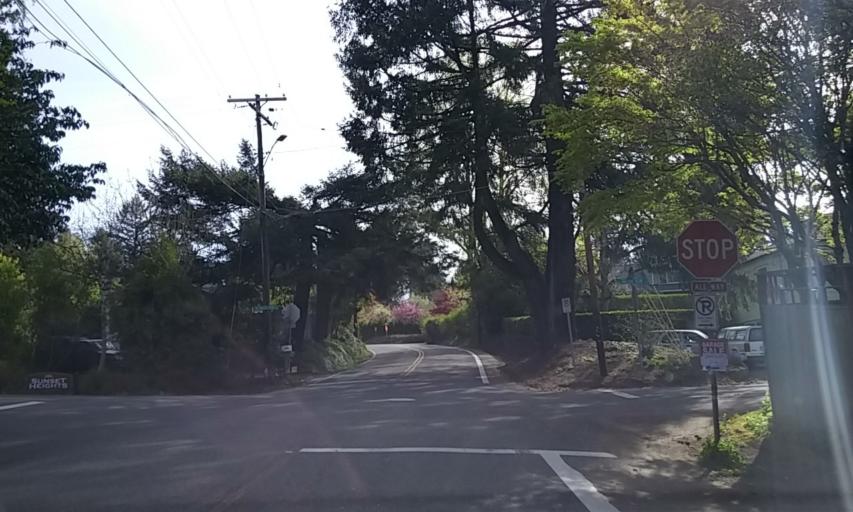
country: US
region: Oregon
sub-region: Washington County
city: West Slope
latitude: 45.5001
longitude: -122.7600
